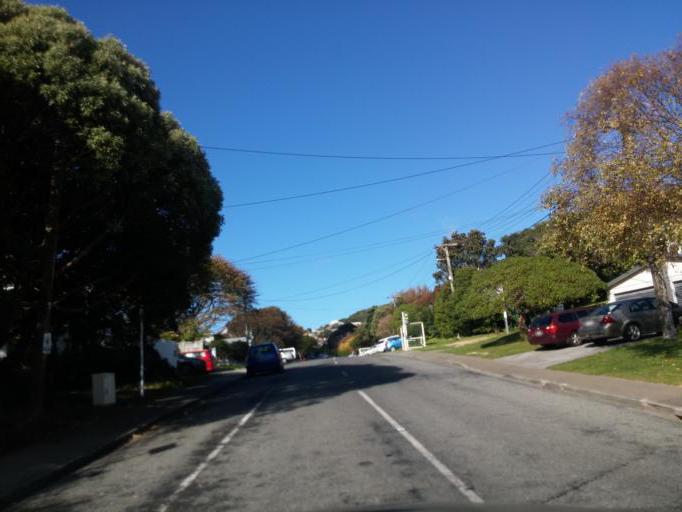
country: NZ
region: Wellington
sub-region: Wellington City
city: Kelburn
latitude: -41.2476
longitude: 174.7753
